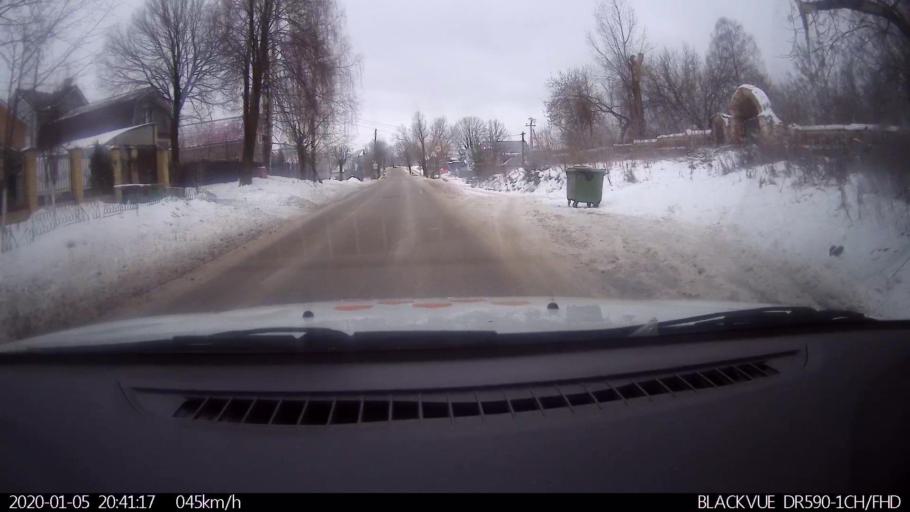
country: RU
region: Nizjnij Novgorod
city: Lukino
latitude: 56.4046
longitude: 43.7289
